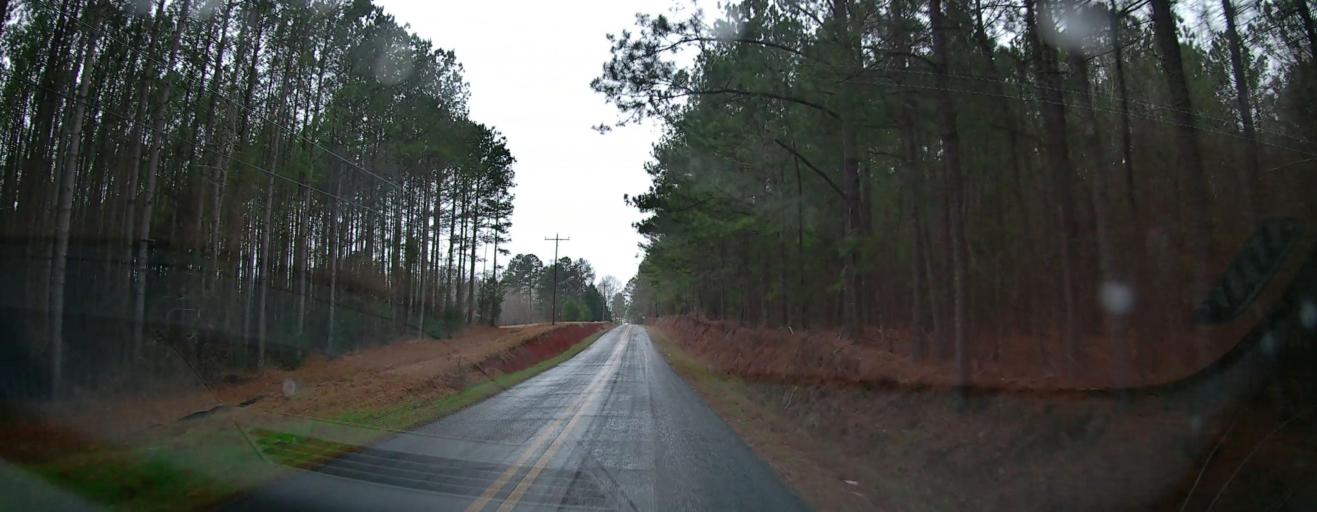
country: US
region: Georgia
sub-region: Monroe County
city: Forsyth
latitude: 33.0773
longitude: -83.8844
